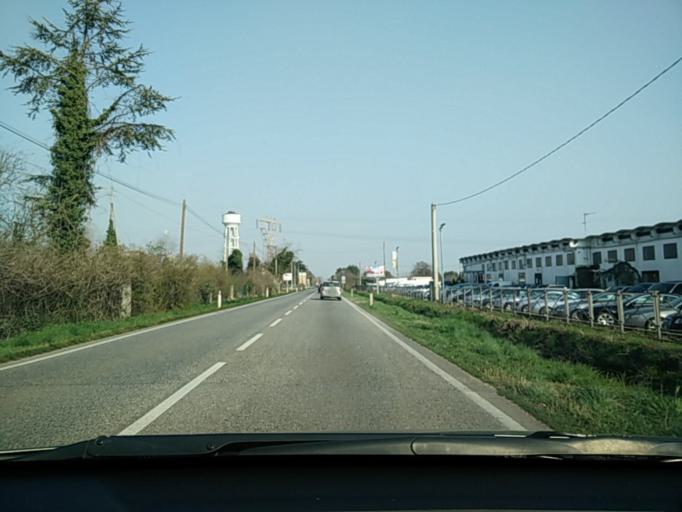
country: IT
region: Veneto
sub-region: Provincia di Treviso
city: Ponzano
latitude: 45.7243
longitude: 12.1797
